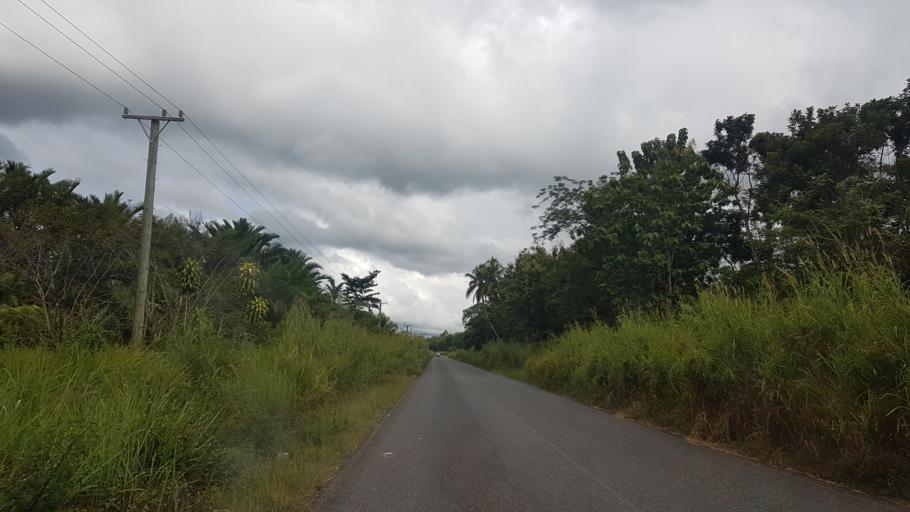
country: PG
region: Northern Province
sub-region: Sohe
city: Popondetta
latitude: -8.7964
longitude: 148.2281
